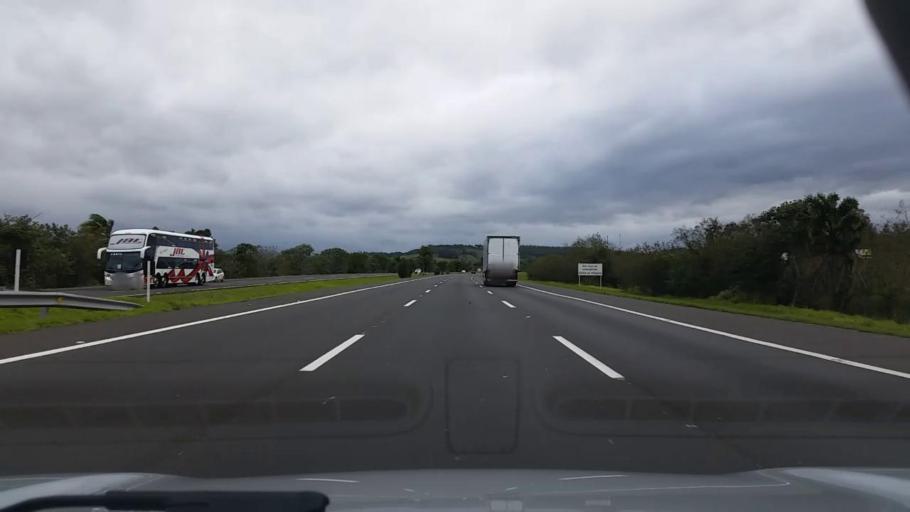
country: BR
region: Rio Grande do Sul
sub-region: Osorio
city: Osorio
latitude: -29.8883
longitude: -50.4573
